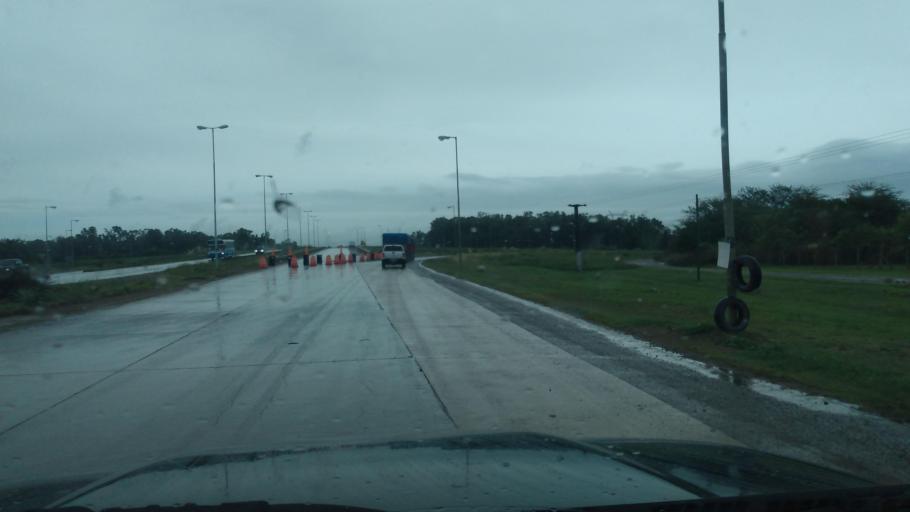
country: AR
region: Buenos Aires
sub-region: Partido de Pilar
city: Pilar
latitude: -34.3928
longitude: -59.0206
